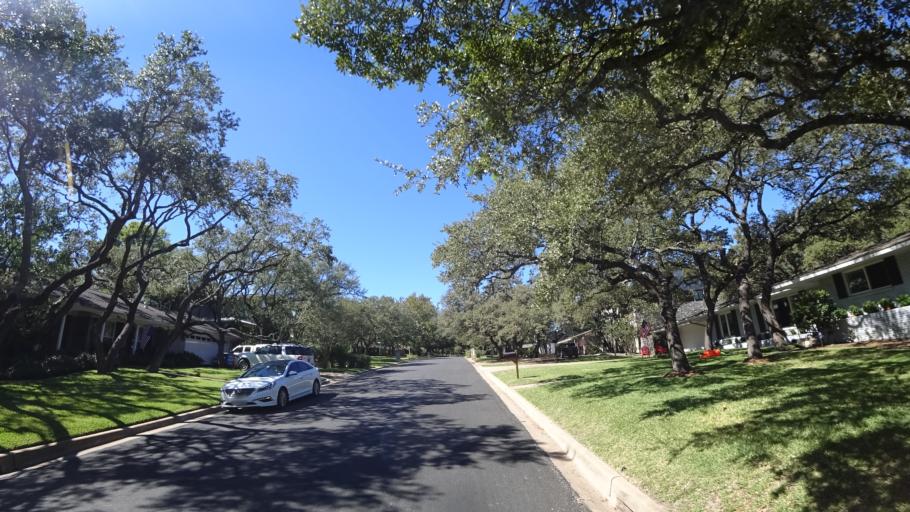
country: US
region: Texas
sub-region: Travis County
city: West Lake Hills
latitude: 30.3245
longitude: -97.7699
